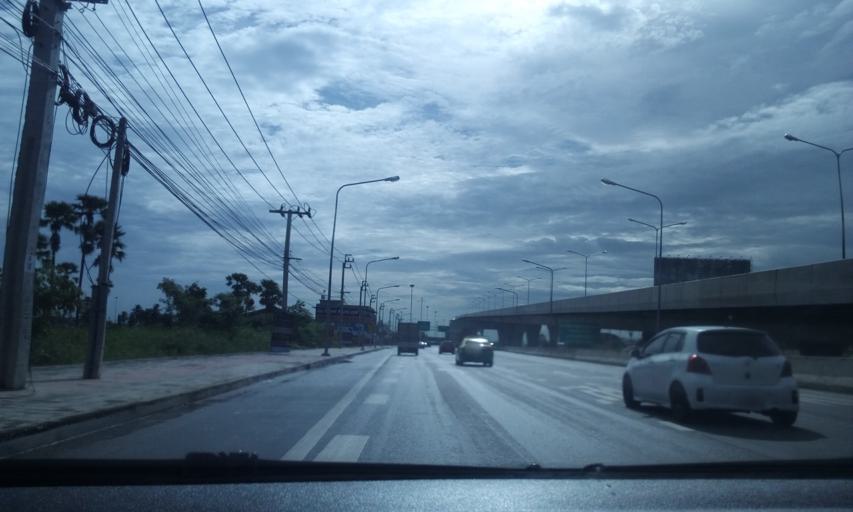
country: TH
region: Nonthaburi
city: Bang Bua Thong
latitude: 13.9265
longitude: 100.4590
